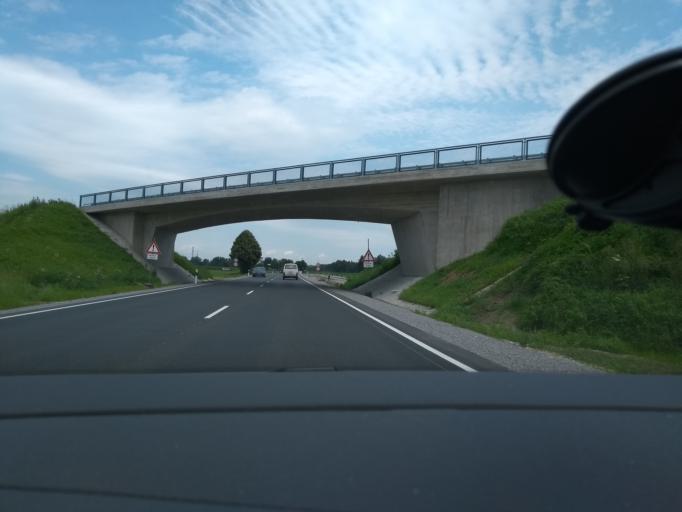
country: DE
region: Bavaria
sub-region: Upper Bavaria
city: Schechen
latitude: 47.9013
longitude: 12.1227
